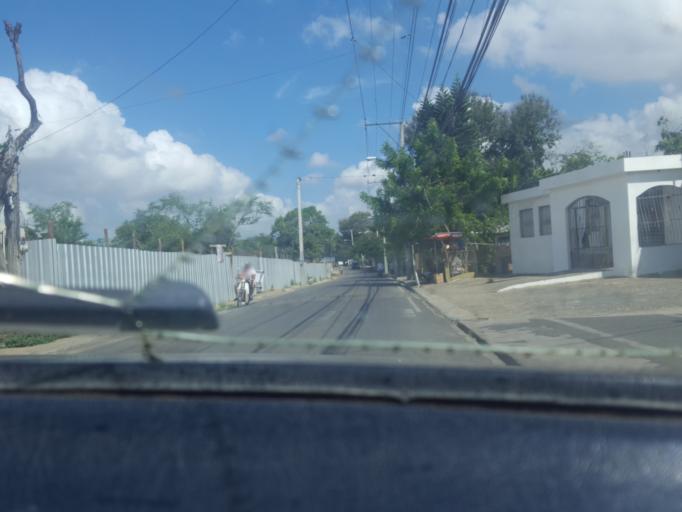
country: DO
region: Santiago
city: Santiago de los Caballeros
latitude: 19.4863
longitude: -70.6990
